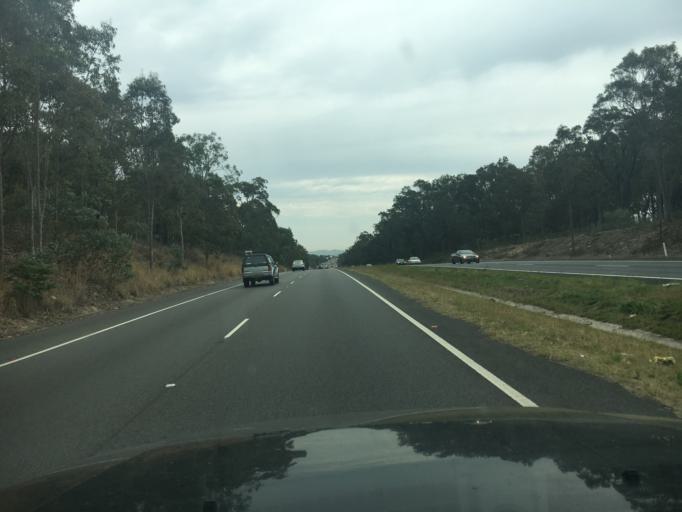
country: AU
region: New South Wales
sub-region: Maitland Municipality
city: East Maitland
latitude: -32.7682
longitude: 151.6023
